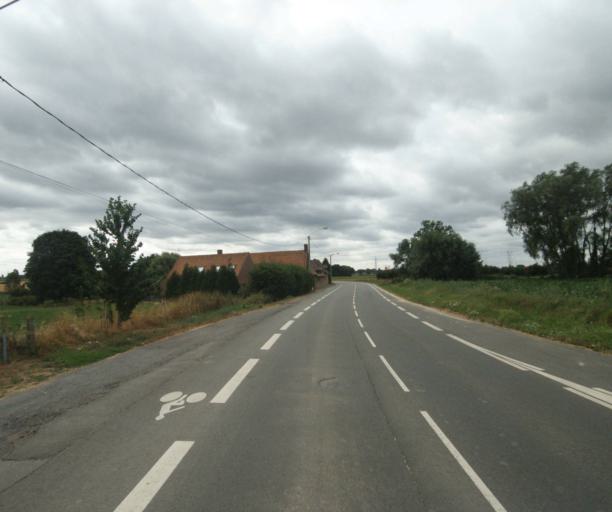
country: FR
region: Nord-Pas-de-Calais
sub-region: Departement du Nord
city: Linselles
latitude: 50.7288
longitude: 3.0807
